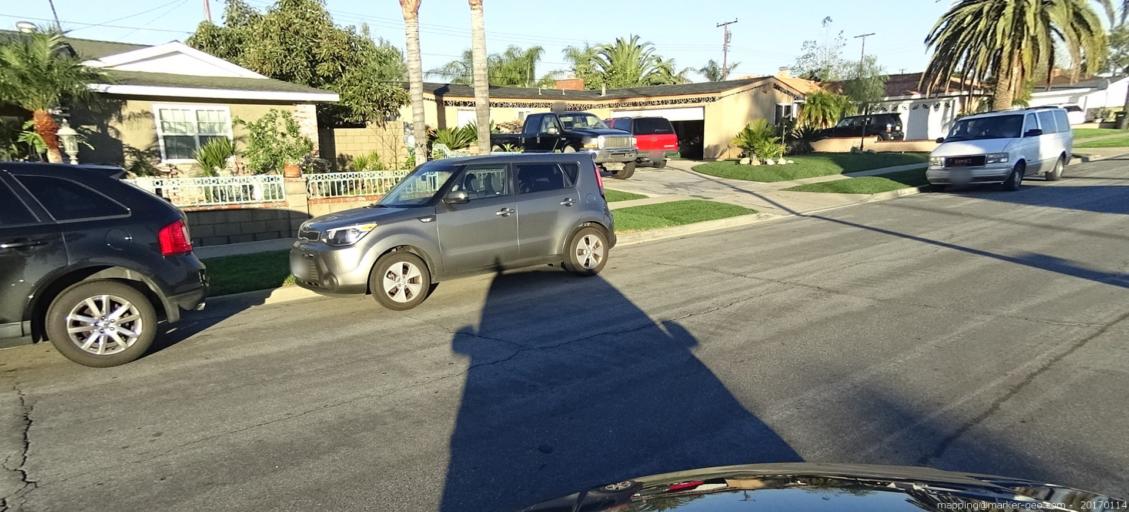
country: US
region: California
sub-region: Orange County
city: Villa Park
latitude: 33.7972
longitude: -117.8078
